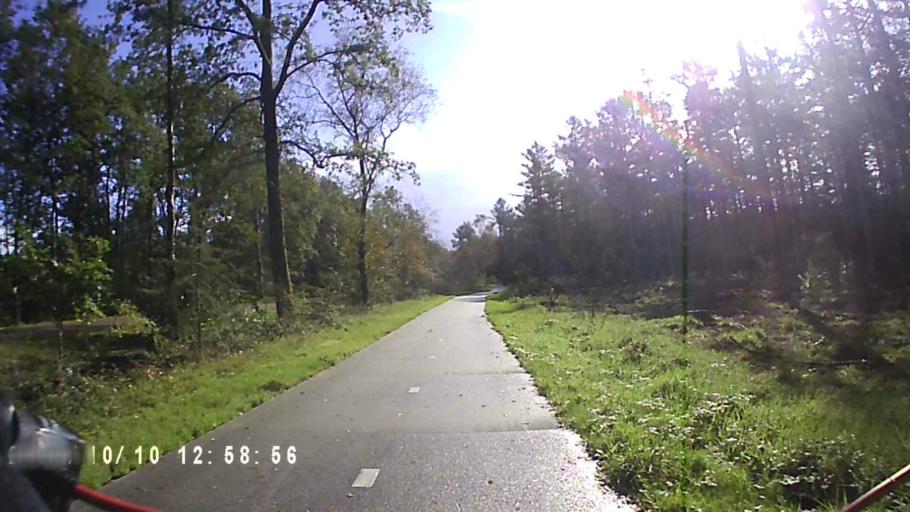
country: NL
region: Drenthe
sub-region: Gemeente Westerveld
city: Dwingeloo
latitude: 52.9006
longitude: 6.2975
